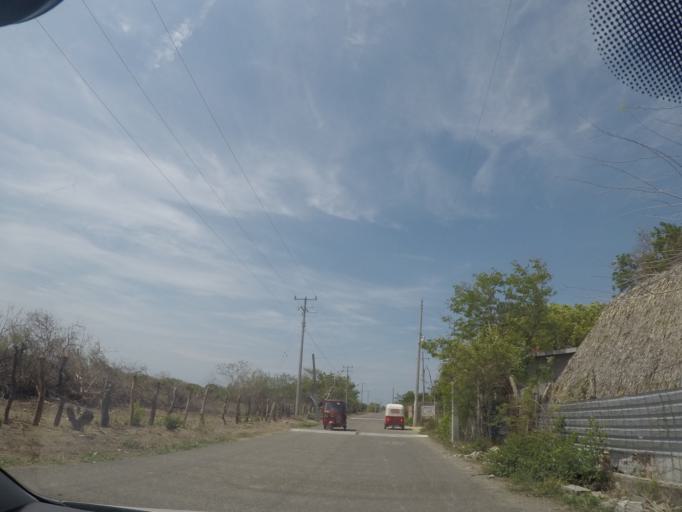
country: MX
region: Oaxaca
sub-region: Salina Cruz
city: Salina Cruz
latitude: 16.2001
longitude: -95.1196
